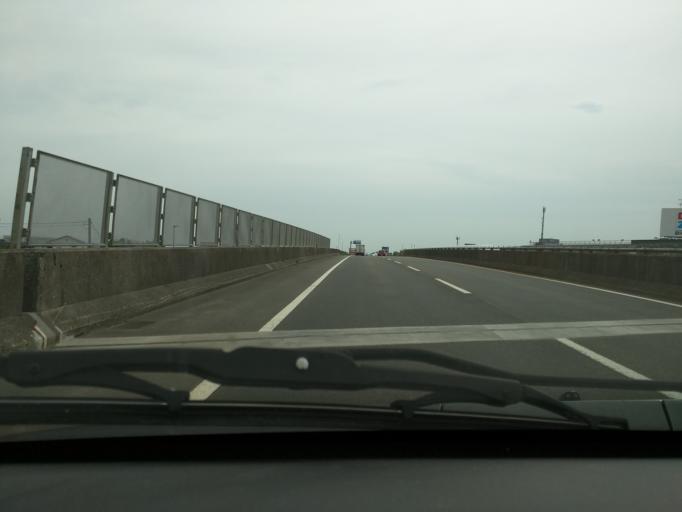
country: JP
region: Niigata
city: Nagaoka
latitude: 37.4520
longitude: 138.8019
